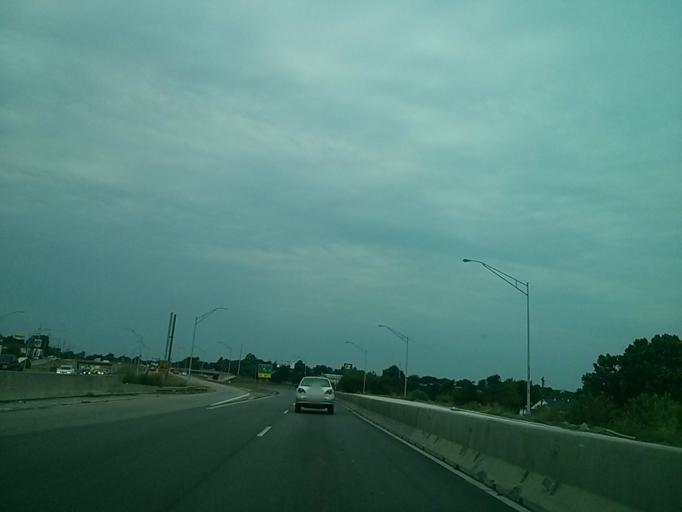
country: US
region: Oklahoma
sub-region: Tulsa County
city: Tulsa
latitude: 36.1629
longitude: -95.8994
